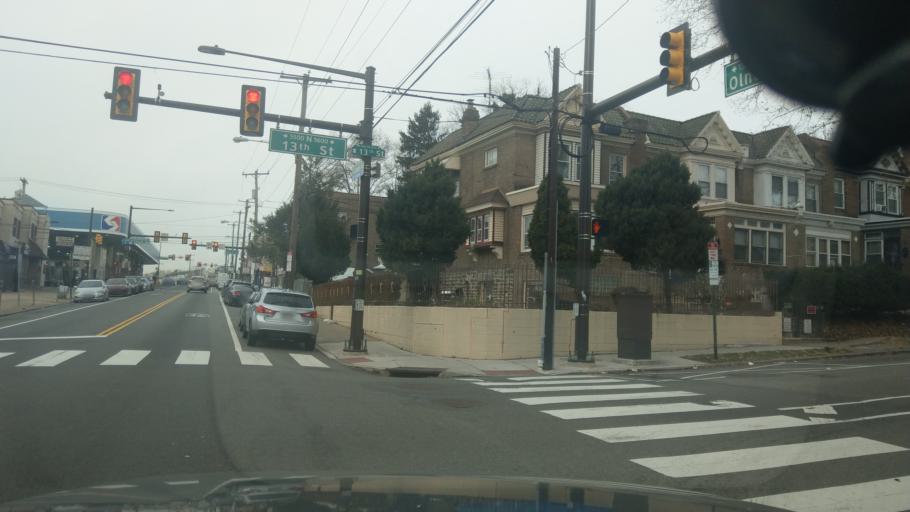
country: US
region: Pennsylvania
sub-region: Montgomery County
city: Wyncote
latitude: 40.0386
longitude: -75.1425
